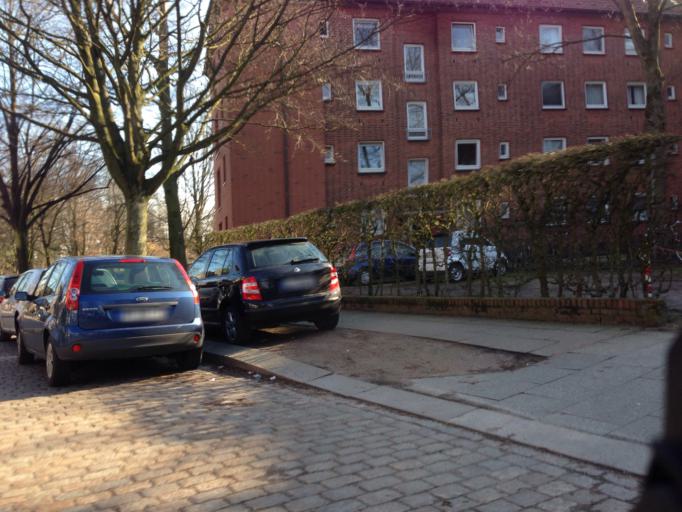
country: DE
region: Hamburg
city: Barmbek-Nord
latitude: 53.5855
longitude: 10.0536
